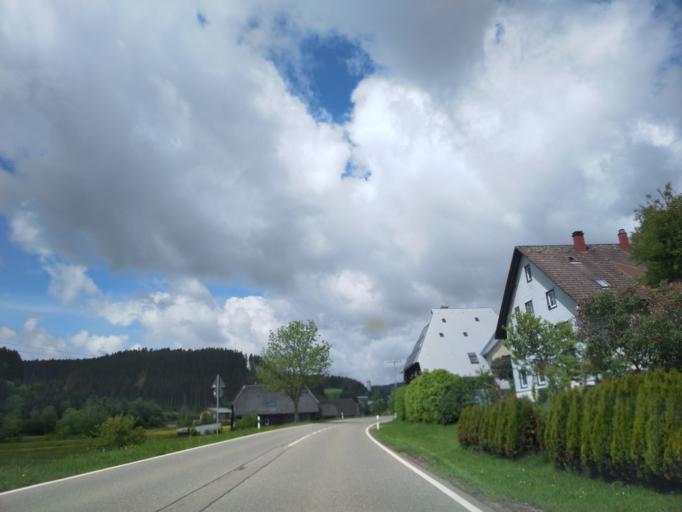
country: DE
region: Baden-Wuerttemberg
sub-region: Freiburg Region
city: Furtwangen im Schwarzwald
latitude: 48.0459
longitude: 8.2304
